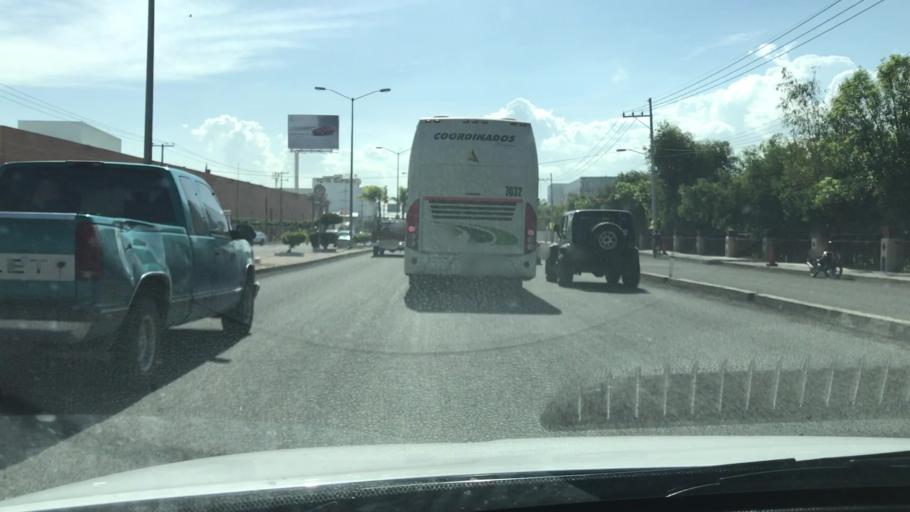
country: MX
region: Guanajuato
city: Celaya
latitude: 20.5162
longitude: -100.7831
